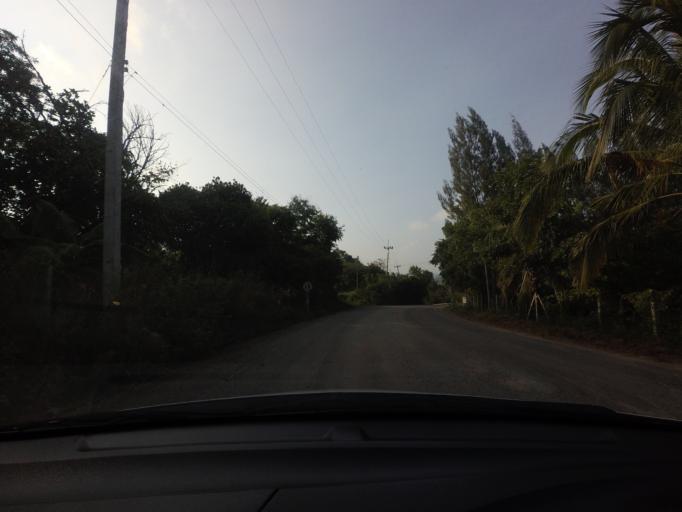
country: TH
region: Nakhon Ratchasima
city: Pak Chong
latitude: 14.5356
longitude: 101.5843
